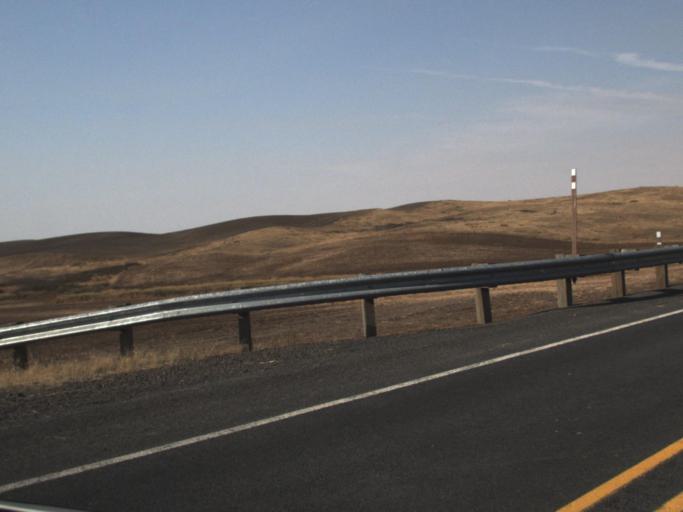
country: US
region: Idaho
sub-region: Benewah County
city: Plummer
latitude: 47.1771
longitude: -117.1894
